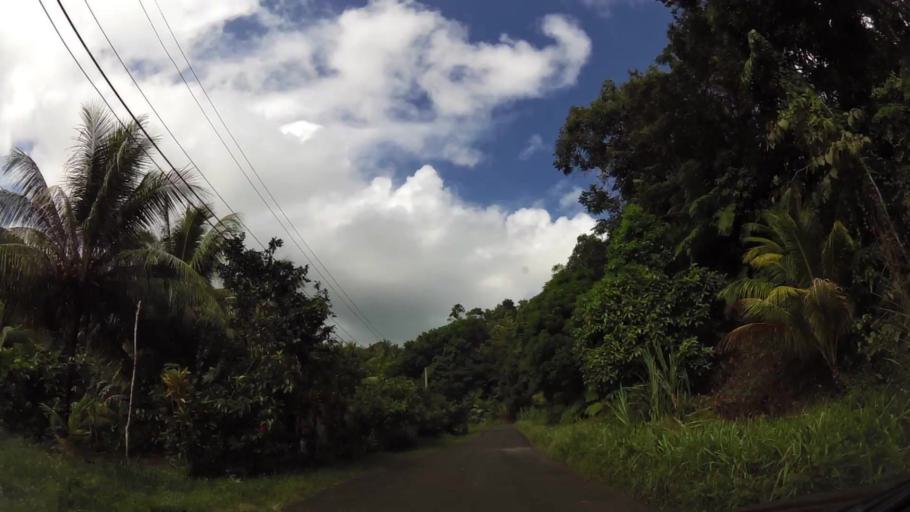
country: DM
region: Saint David
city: Castle Bruce
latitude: 15.4656
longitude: -61.2530
